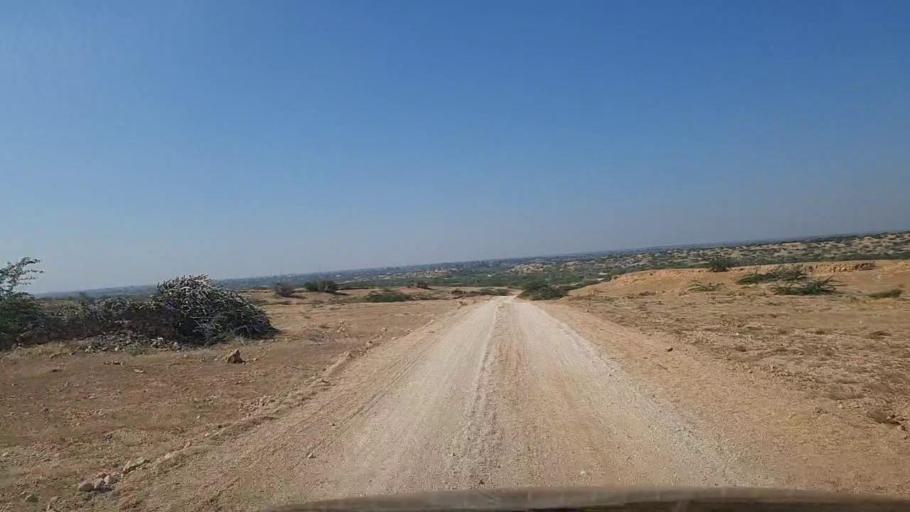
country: PK
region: Sindh
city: Thatta
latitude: 24.6223
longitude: 67.8494
